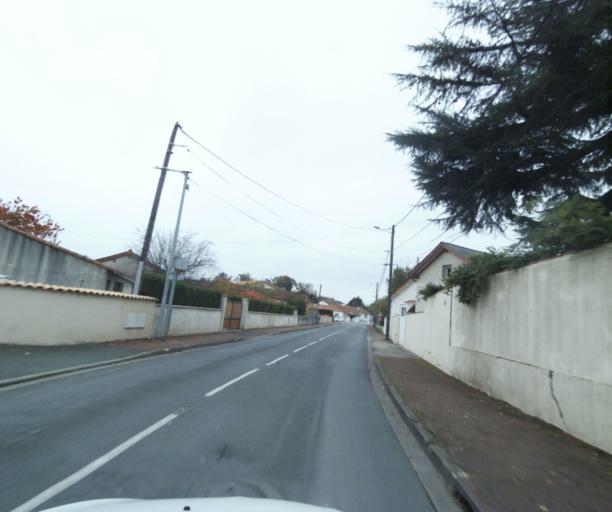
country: FR
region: Poitou-Charentes
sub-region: Departement de la Charente-Maritime
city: Saintes
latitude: 45.7392
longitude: -0.6147
